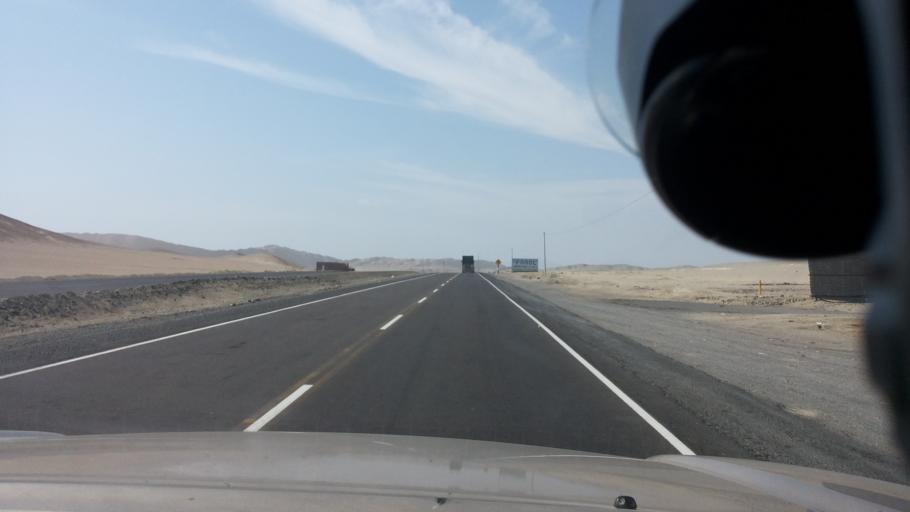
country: PE
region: Ancash
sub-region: Provincia de Casma
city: Casma
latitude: -9.5376
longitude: -78.2747
